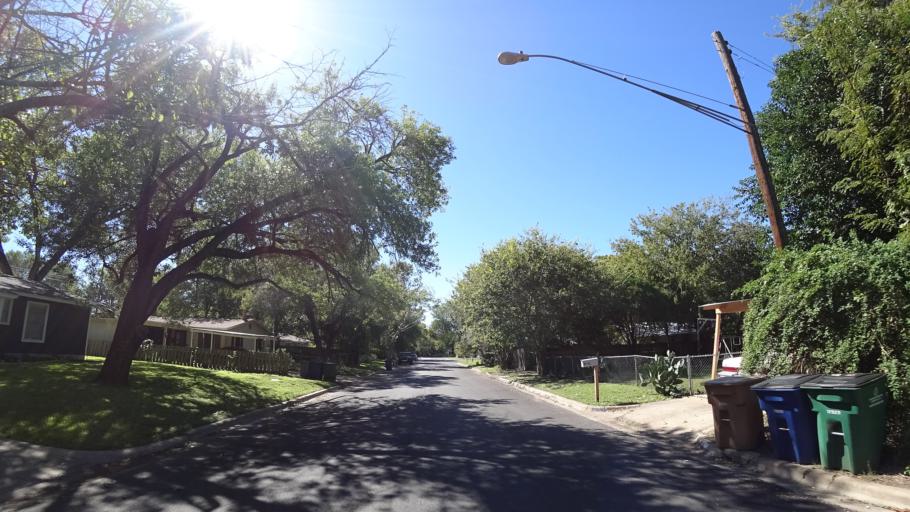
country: US
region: Texas
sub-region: Travis County
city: Austin
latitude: 30.2377
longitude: -97.7703
